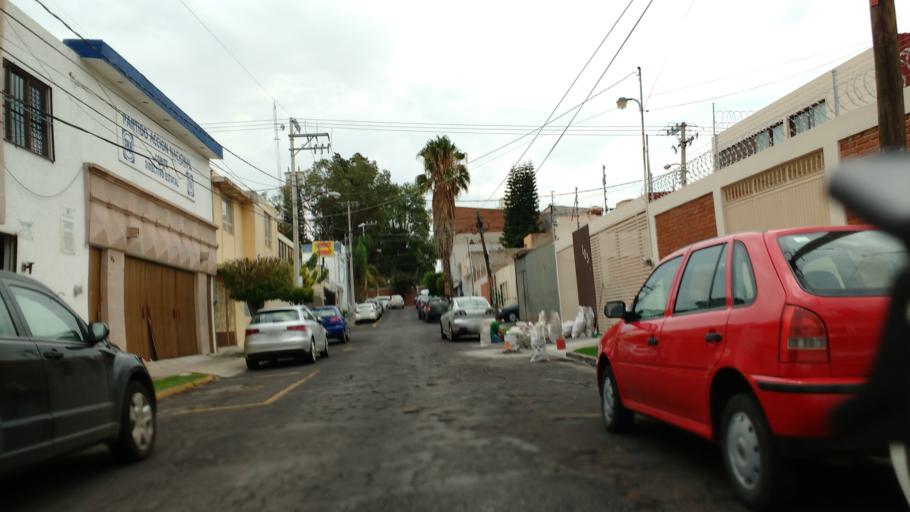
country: MX
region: Michoacan
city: Morelia
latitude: 19.6923
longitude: -101.1758
